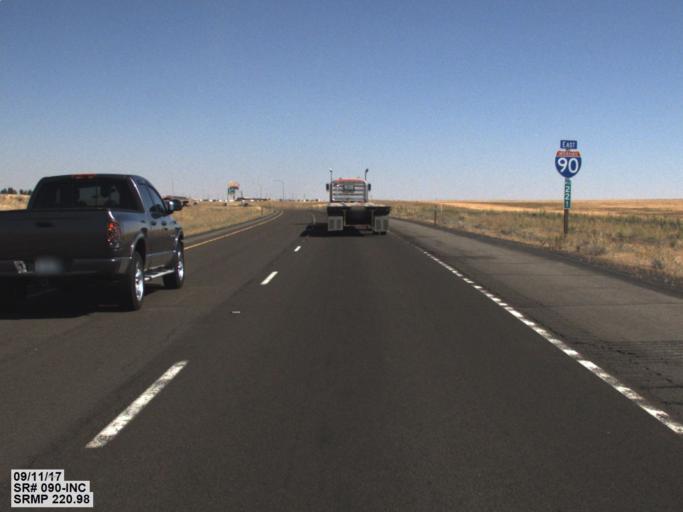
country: US
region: Washington
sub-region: Adams County
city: Ritzville
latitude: 47.1113
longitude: -118.3850
